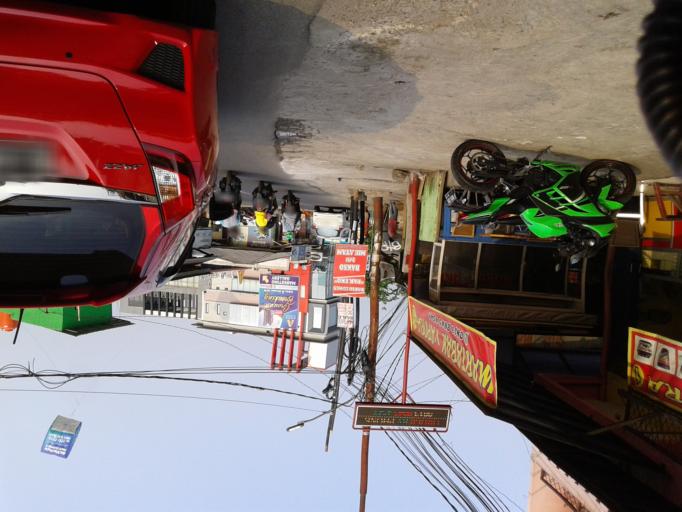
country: ID
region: Banten
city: South Tangerang
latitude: -6.2912
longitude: 106.7305
